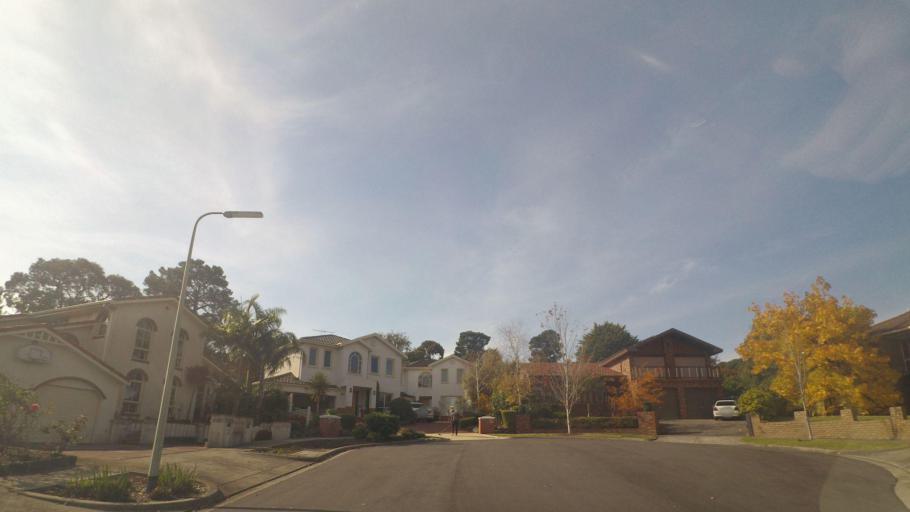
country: AU
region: Victoria
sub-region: Manningham
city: Doncaster East
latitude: -37.7692
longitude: 145.1497
